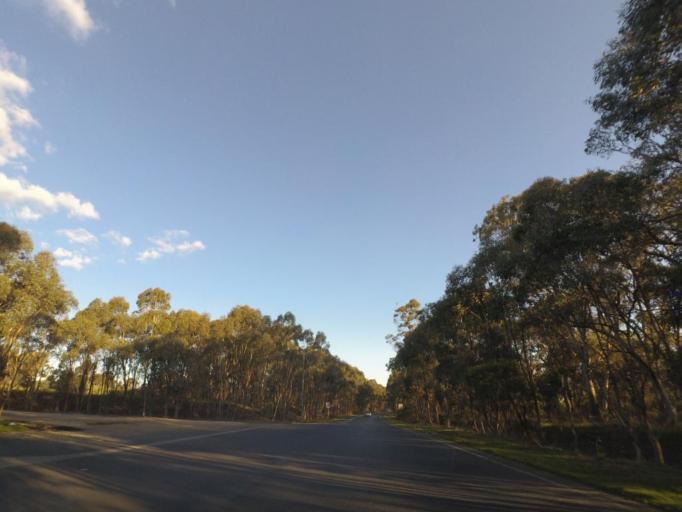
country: AU
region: Victoria
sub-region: Murrindindi
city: Kinglake West
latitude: -37.0646
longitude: 145.1019
